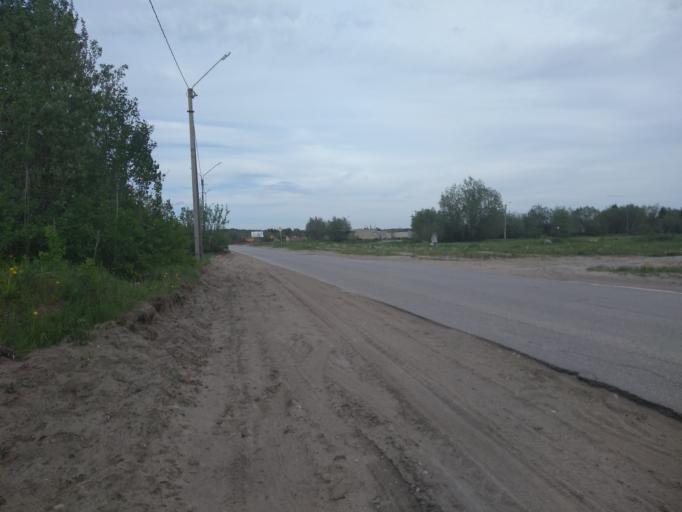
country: RU
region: Komi Republic
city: Pechora
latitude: 65.1434
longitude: 57.2456
